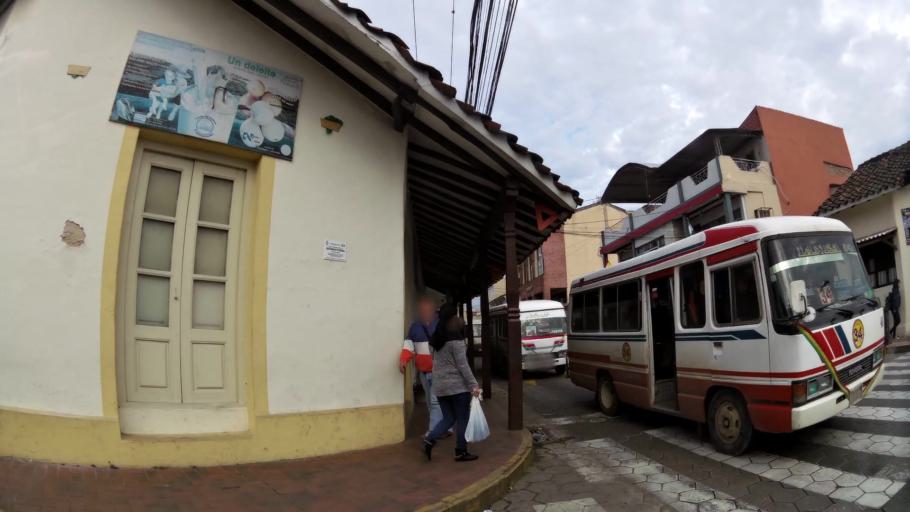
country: BO
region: Santa Cruz
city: Santa Cruz de la Sierra
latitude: -17.7873
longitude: -63.1787
